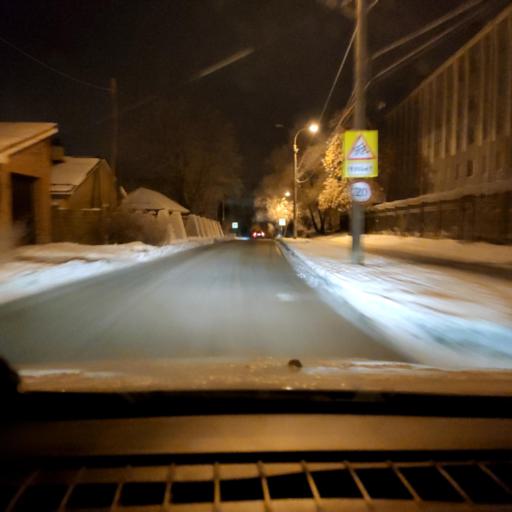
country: RU
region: Samara
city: Novosemeykino
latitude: 53.3443
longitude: 50.2282
